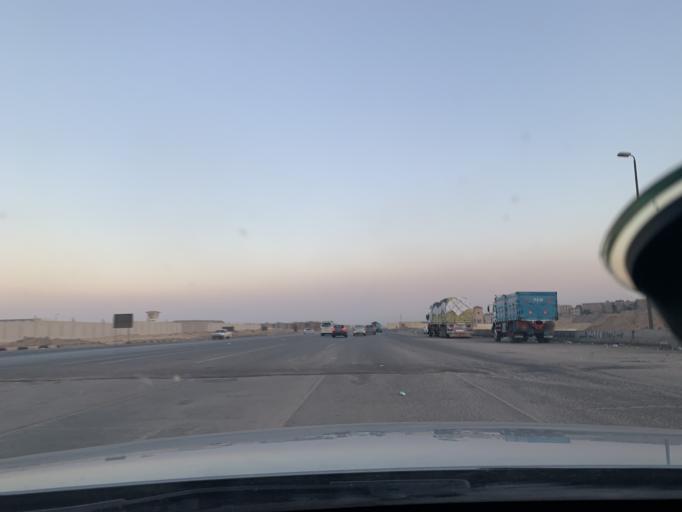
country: EG
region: Muhafazat al Qalyubiyah
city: Al Khankah
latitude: 30.1972
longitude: 31.4216
